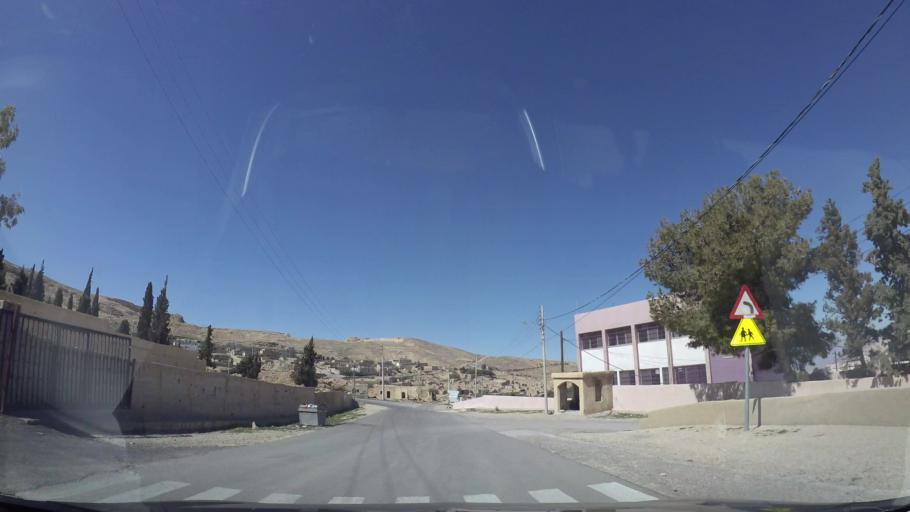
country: JO
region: Tafielah
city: At Tafilah
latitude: 30.8412
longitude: 35.5678
